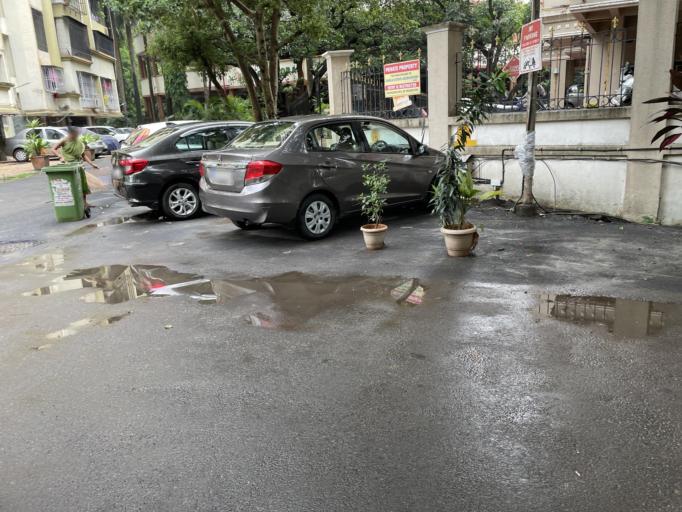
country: IN
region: Maharashtra
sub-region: Mumbai Suburban
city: Borivli
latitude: 19.2288
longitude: 72.8665
